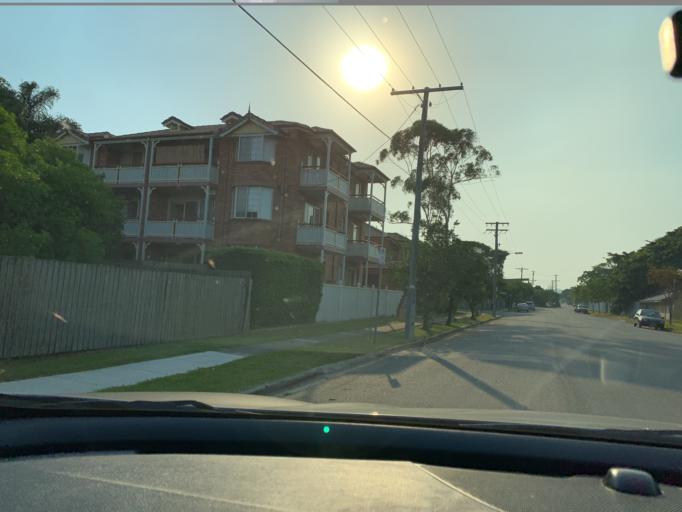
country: AU
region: Queensland
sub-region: Brisbane
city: Ascot
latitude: -27.4293
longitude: 153.0780
